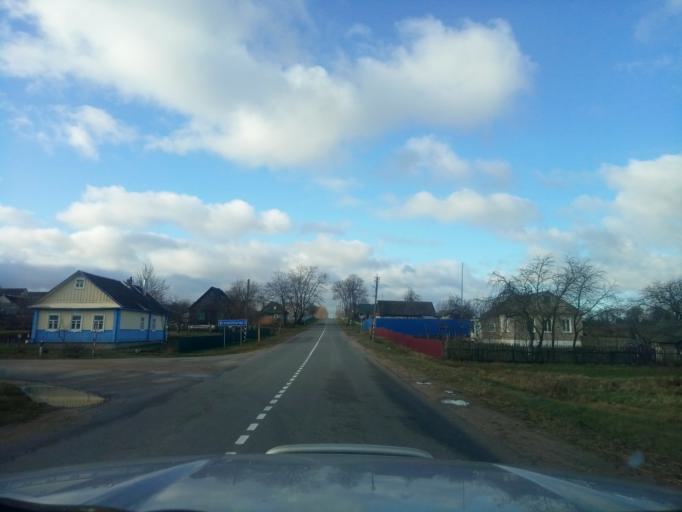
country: BY
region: Minsk
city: Tsimkavichy
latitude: 53.1752
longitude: 26.9679
